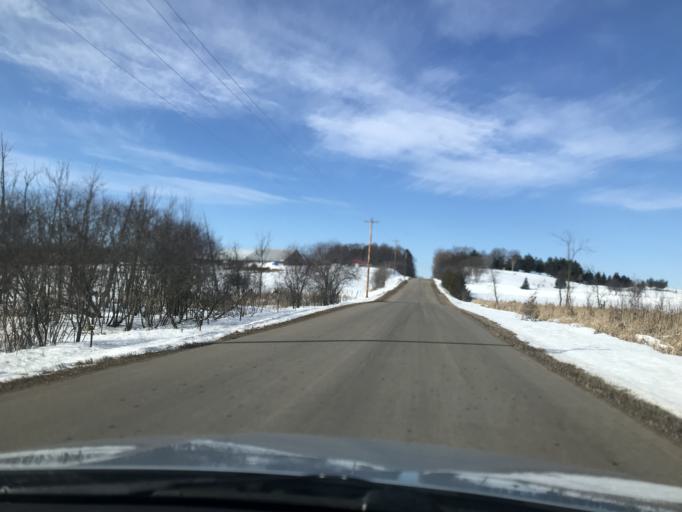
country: US
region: Wisconsin
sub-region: Oconto County
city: Gillett
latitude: 44.9618
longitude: -88.2963
